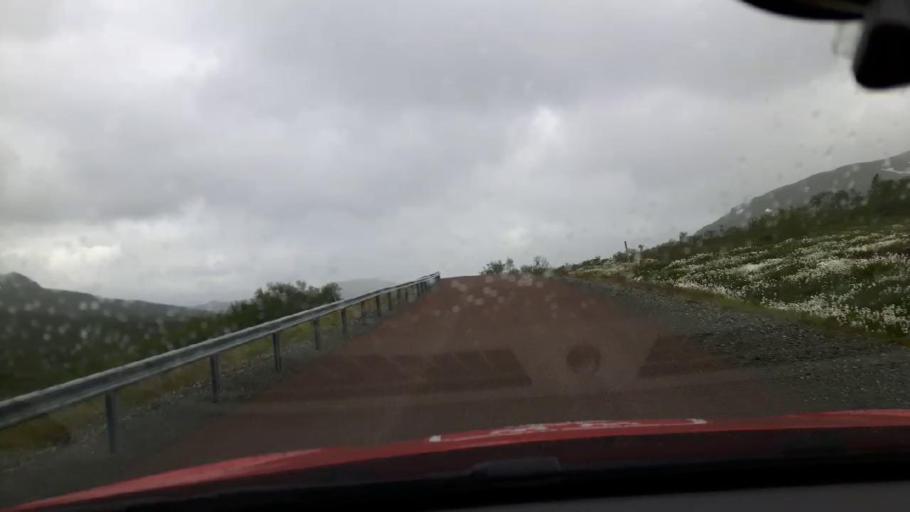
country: NO
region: Nord-Trondelag
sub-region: Meraker
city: Meraker
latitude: 63.1999
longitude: 12.3901
